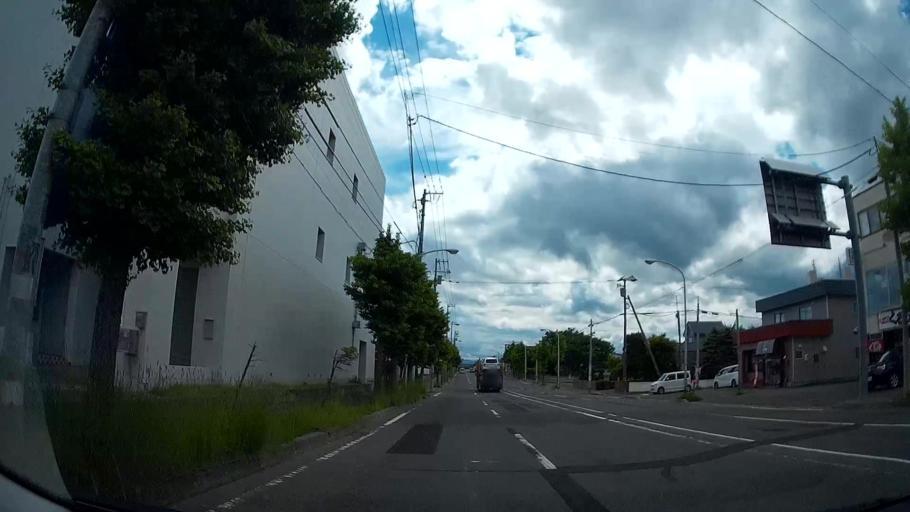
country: JP
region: Hokkaido
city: Kitahiroshima
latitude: 42.8825
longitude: 141.5750
